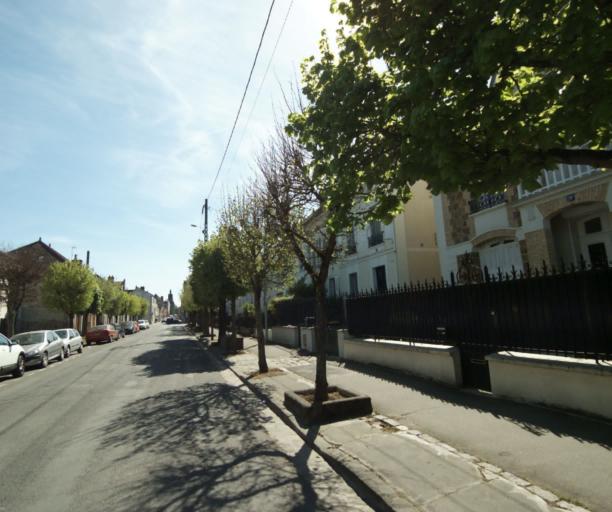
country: FR
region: Ile-de-France
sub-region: Departement de Seine-et-Marne
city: Nangis
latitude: 48.5591
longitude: 3.0135
